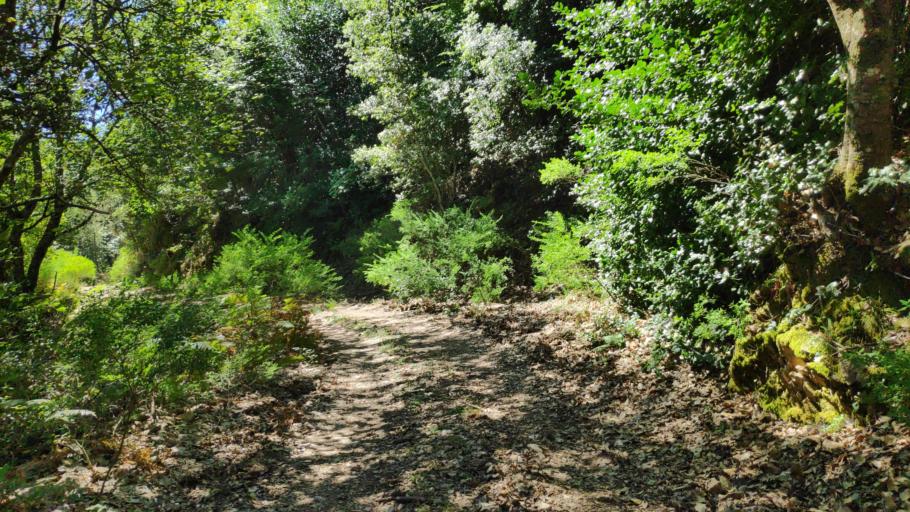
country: IT
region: Calabria
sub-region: Provincia di Vibo-Valentia
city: Nardodipace
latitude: 38.4795
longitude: 16.3867
